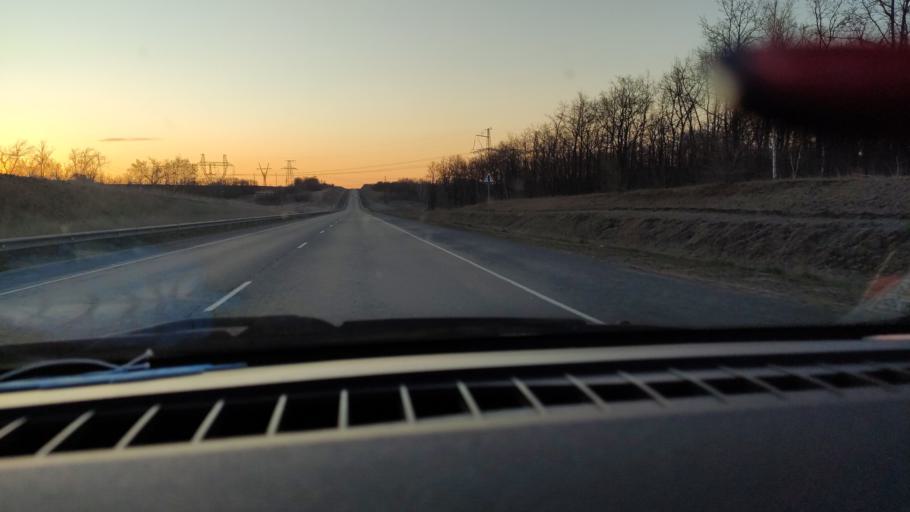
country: RU
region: Saratov
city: Yelshanka
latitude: 51.8234
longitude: 46.3147
